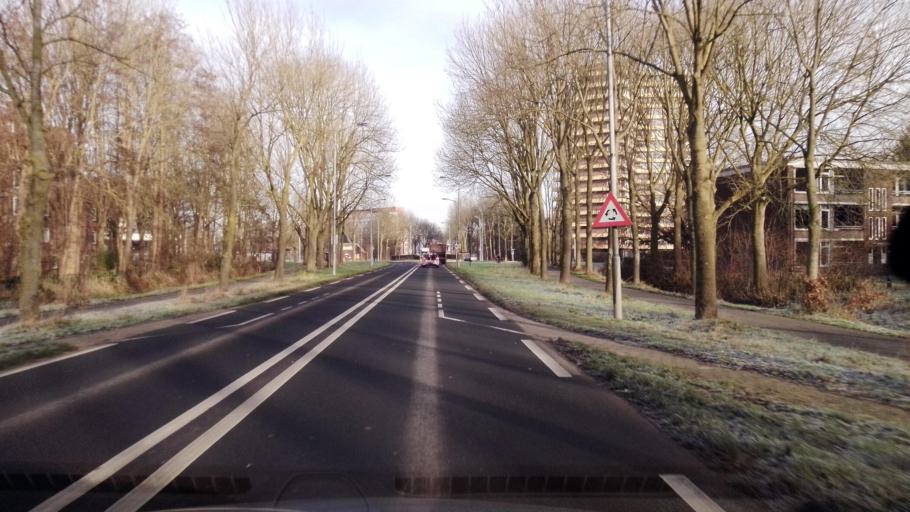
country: NL
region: Gelderland
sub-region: Gemeente Wageningen
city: Wageningen
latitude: 51.9651
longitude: 5.6507
